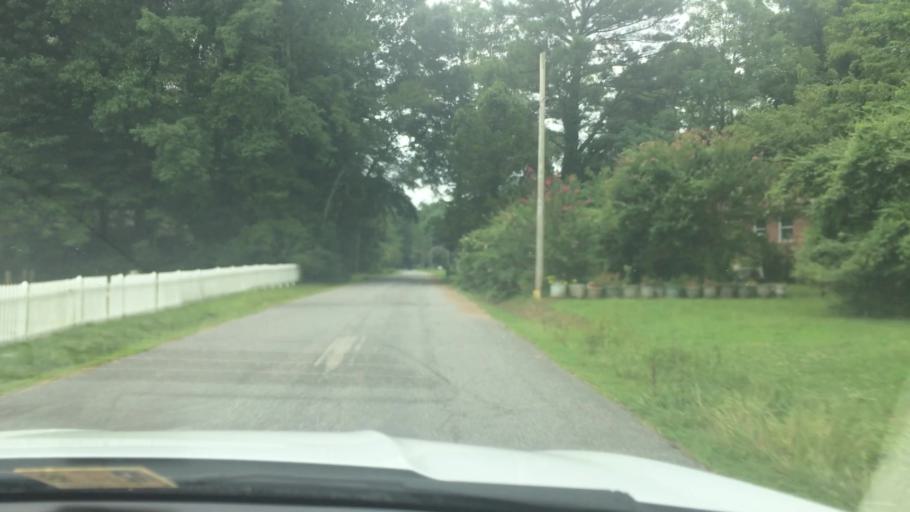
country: US
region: Virginia
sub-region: York County
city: Yorktown
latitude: 37.2321
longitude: -76.5461
